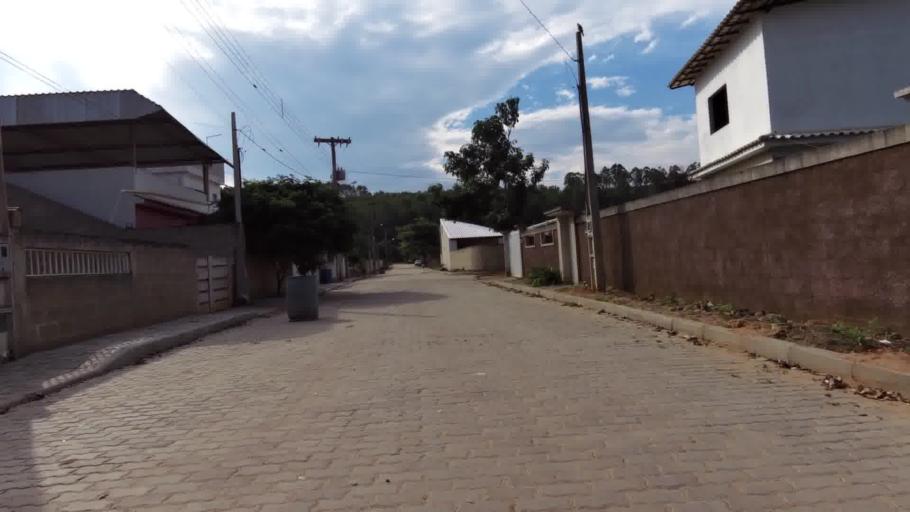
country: BR
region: Espirito Santo
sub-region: Piuma
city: Piuma
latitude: -20.8369
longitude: -40.7326
